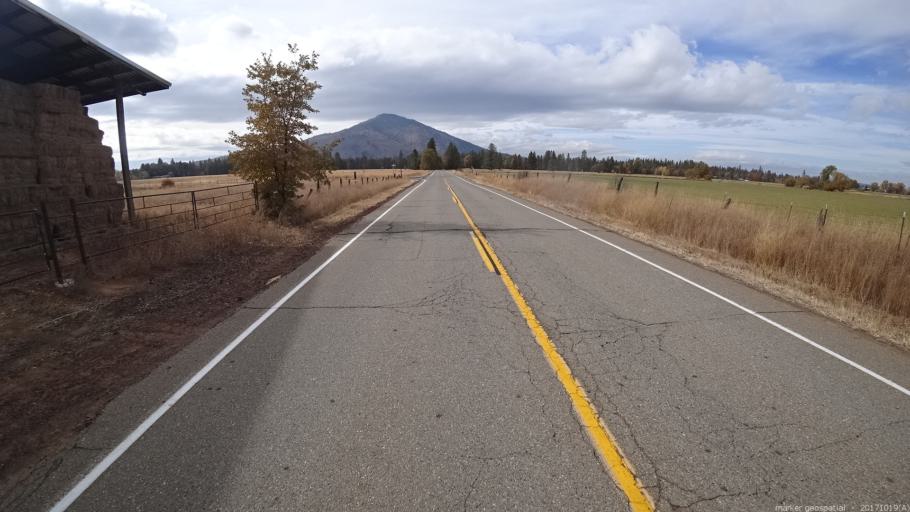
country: US
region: California
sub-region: Shasta County
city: Burney
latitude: 41.0798
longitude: -121.5083
